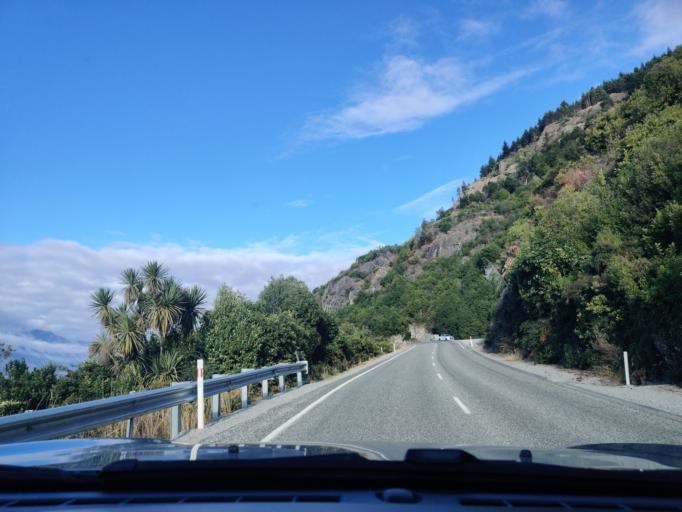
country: NZ
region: Otago
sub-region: Queenstown-Lakes District
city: Queenstown
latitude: -45.0537
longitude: 168.6172
